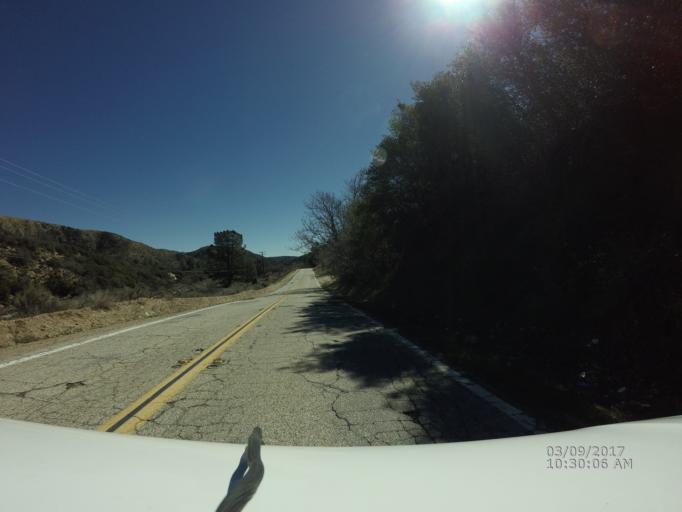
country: US
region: California
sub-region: Los Angeles County
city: Green Valley
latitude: 34.6916
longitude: -118.4871
